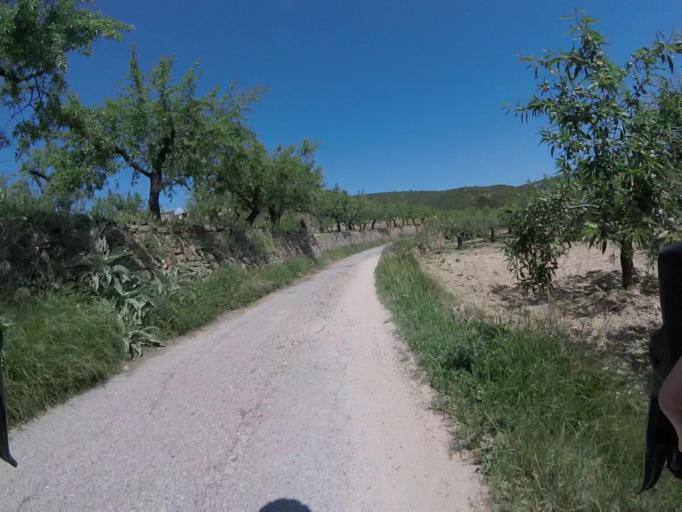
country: ES
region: Valencia
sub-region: Provincia de Castello
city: Sierra-Engarceran
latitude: 40.2486
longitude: -0.0297
